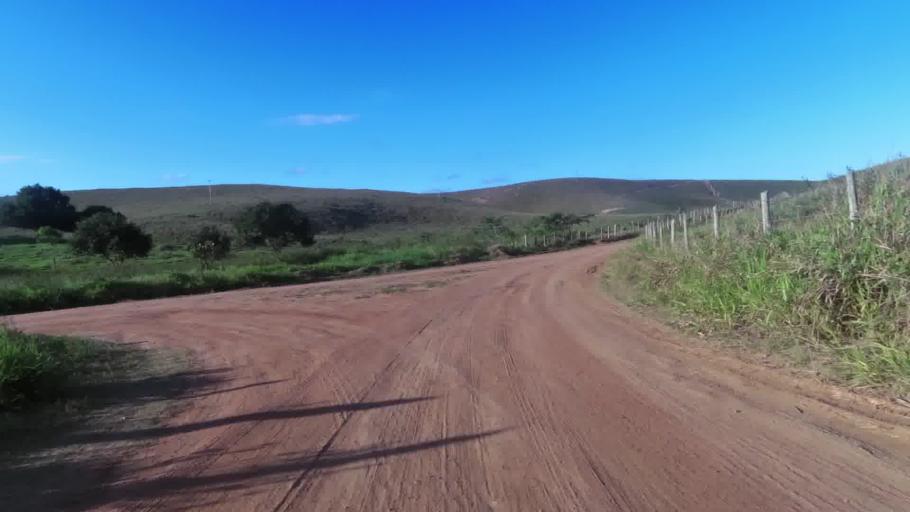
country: BR
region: Espirito Santo
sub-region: Marataizes
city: Marataizes
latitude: -21.1326
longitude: -41.0193
